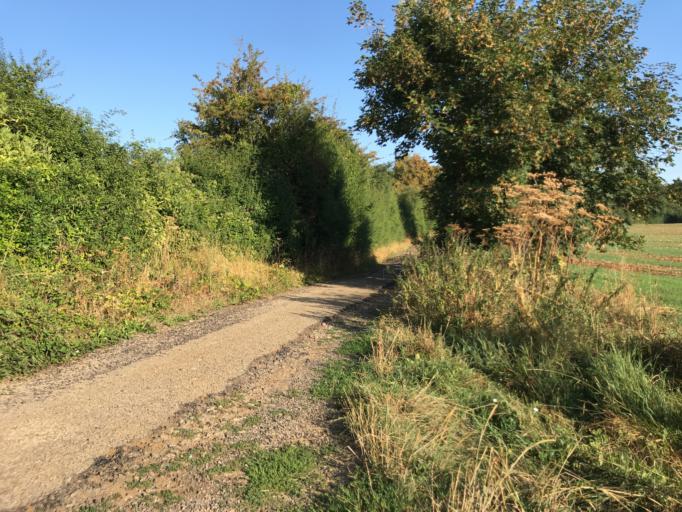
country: LU
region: Luxembourg
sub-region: Canton d'Esch-sur-Alzette
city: Niedercorn
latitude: 49.5331
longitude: 5.8736
